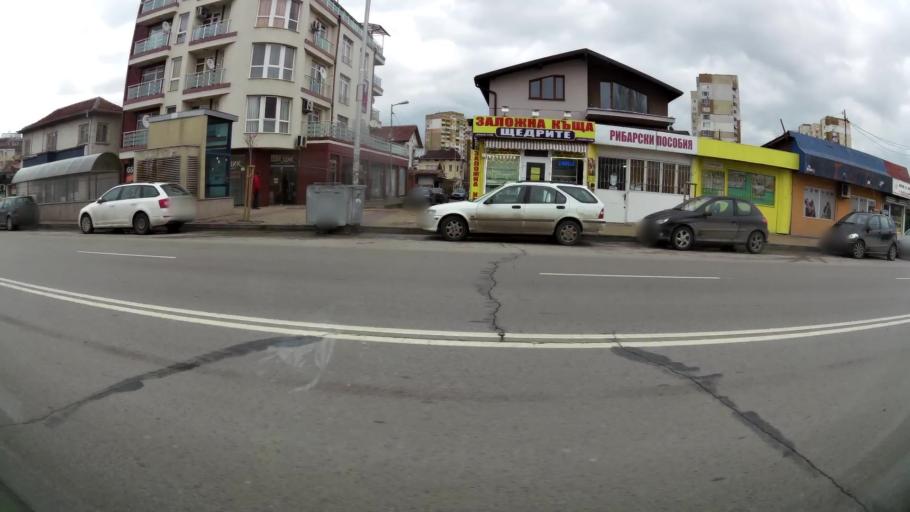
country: BG
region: Sofia-Capital
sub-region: Stolichna Obshtina
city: Sofia
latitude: 42.7337
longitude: 23.2947
